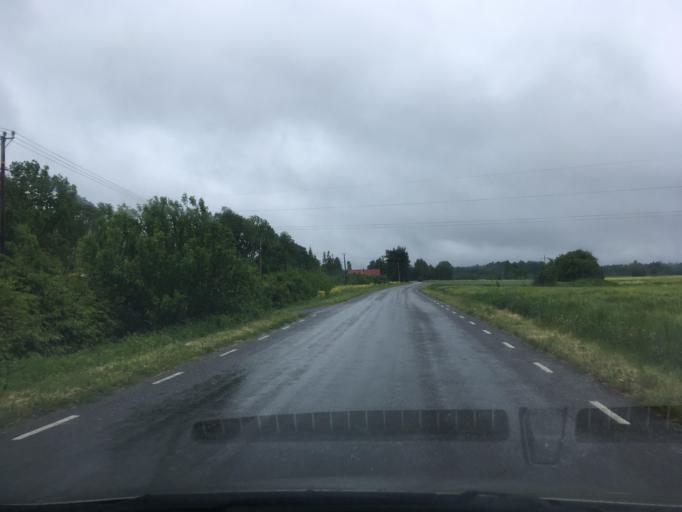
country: EE
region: Laeaene
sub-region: Lihula vald
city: Lihula
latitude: 58.6613
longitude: 23.7712
